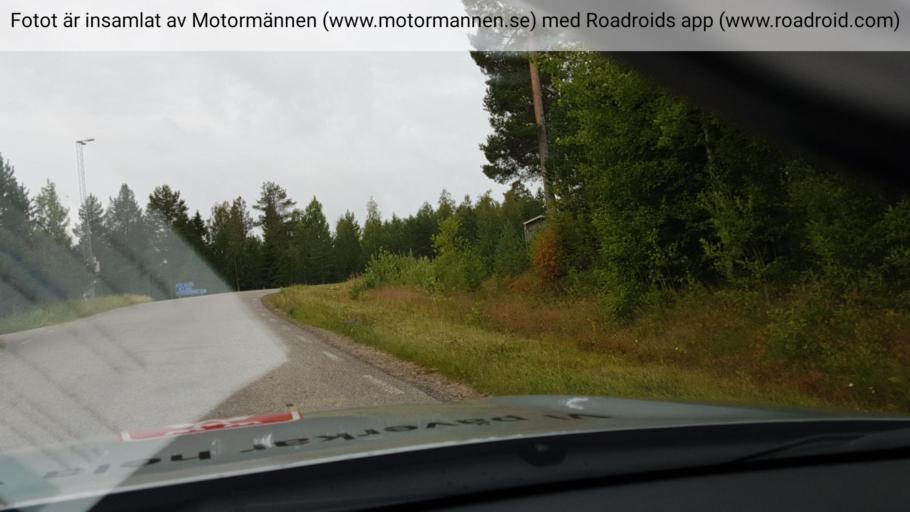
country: SE
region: Norrbotten
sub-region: Bodens Kommun
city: Saevast
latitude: 65.6650
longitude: 21.6646
